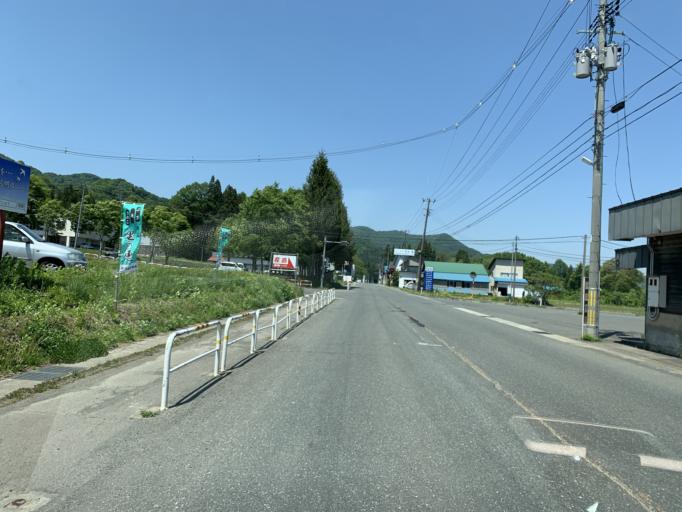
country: JP
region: Akita
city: Yokotemachi
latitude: 39.4333
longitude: 140.7510
